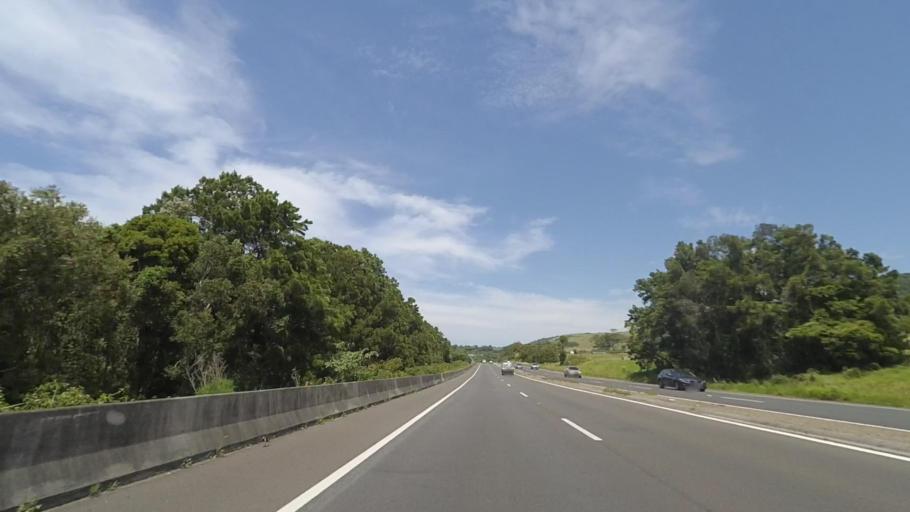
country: AU
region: New South Wales
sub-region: Kiama
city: Kiama
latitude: -34.6844
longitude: 150.8443
